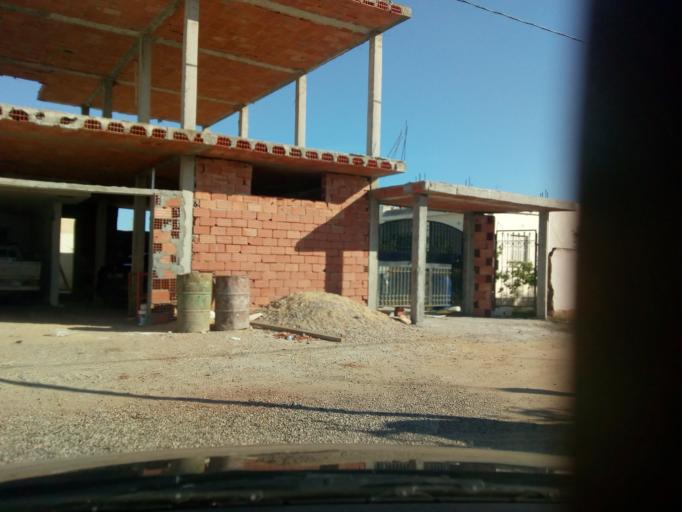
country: TN
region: Safaqis
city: Sfax
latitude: 34.7276
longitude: 10.6259
